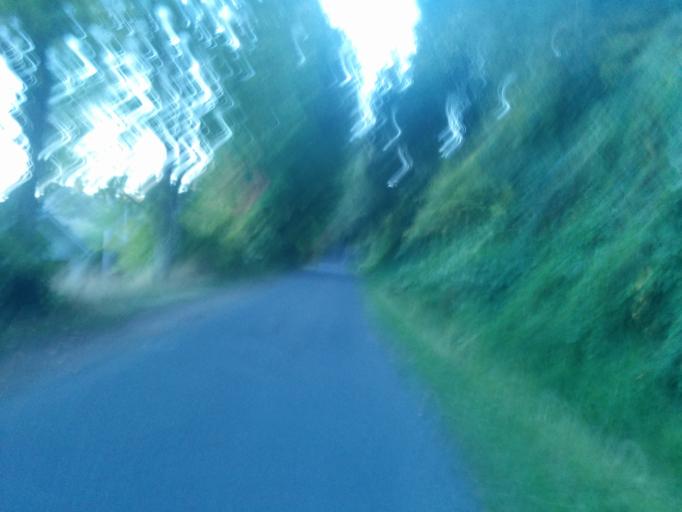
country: US
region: Washington
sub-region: King County
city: Lake Forest Park
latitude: 47.7240
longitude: -122.2813
